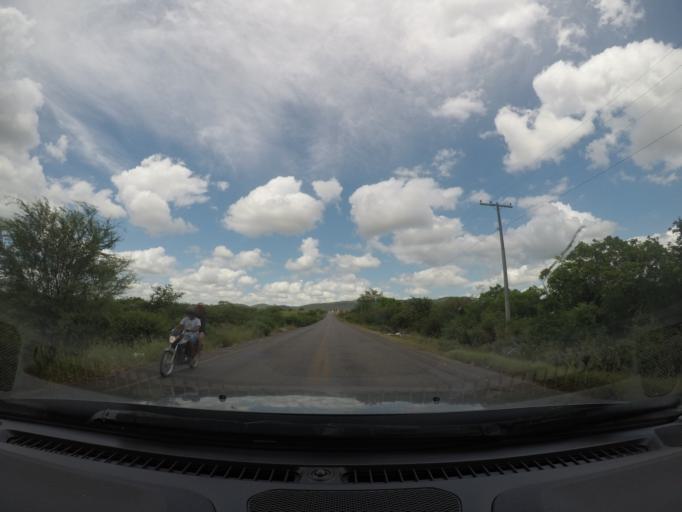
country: BR
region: Bahia
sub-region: Ipira
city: Ipira
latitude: -12.1709
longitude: -39.7531
